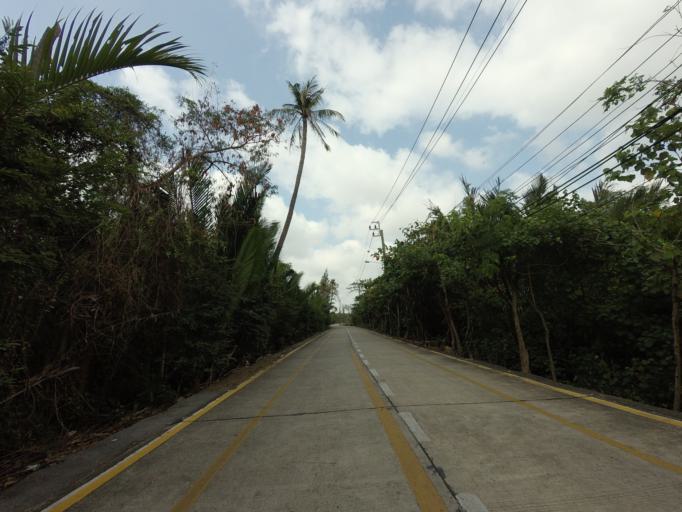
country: TH
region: Samut Prakan
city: Phra Pradaeng
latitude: 13.6614
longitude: 100.5624
